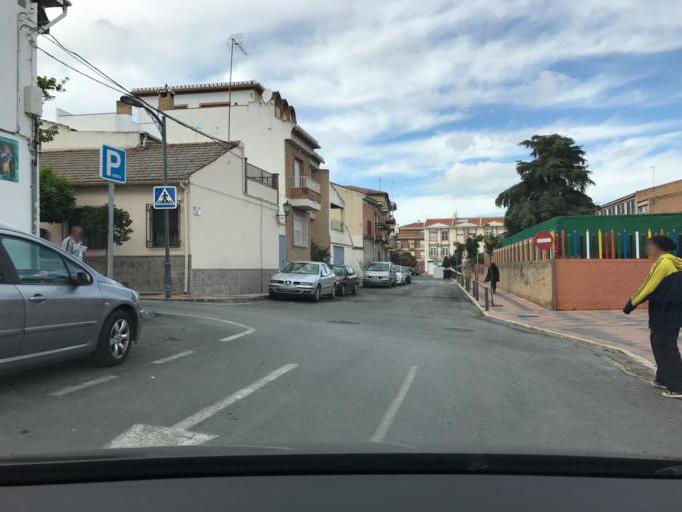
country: ES
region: Andalusia
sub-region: Provincia de Granada
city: Armilla
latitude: 37.1436
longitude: -3.6228
